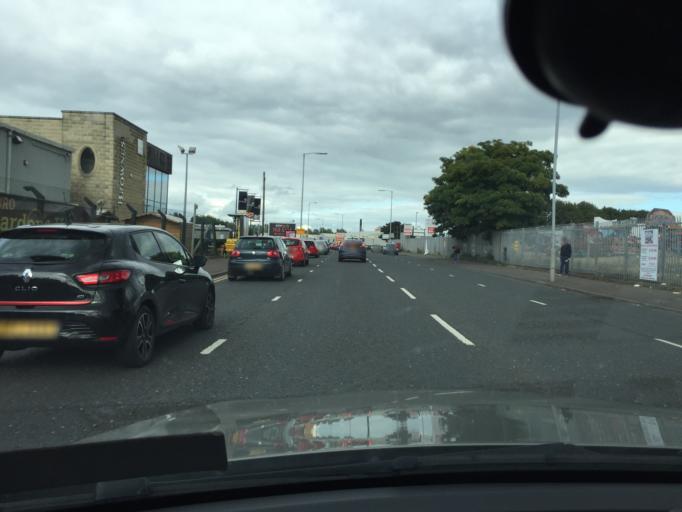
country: GB
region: Northern Ireland
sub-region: City of Belfast
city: Belfast
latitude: 54.5755
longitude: -5.9657
